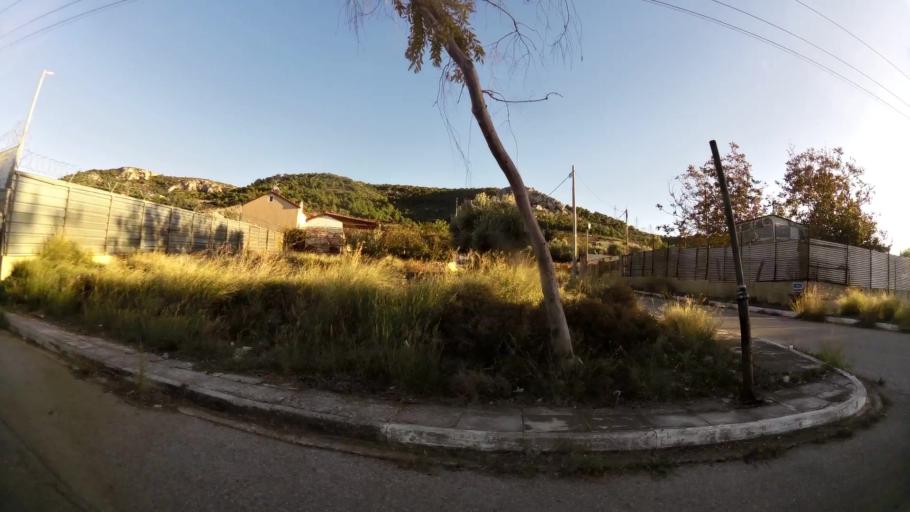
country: GR
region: Attica
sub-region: Nomarchia Athinas
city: Skaramangas
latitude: 38.0324
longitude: 23.6243
